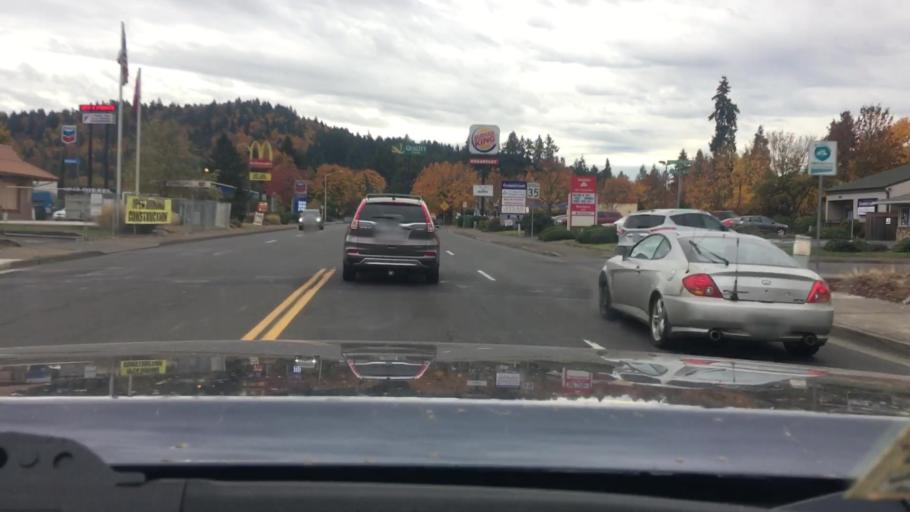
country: US
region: Oregon
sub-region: Lane County
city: Cottage Grove
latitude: 43.8040
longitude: -123.0454
